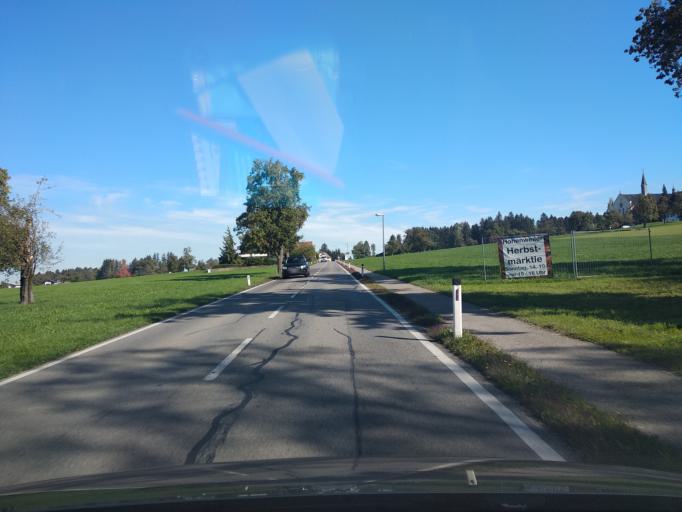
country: DE
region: Bavaria
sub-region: Swabia
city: Sigmarszell
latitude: 47.5684
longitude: 9.7677
